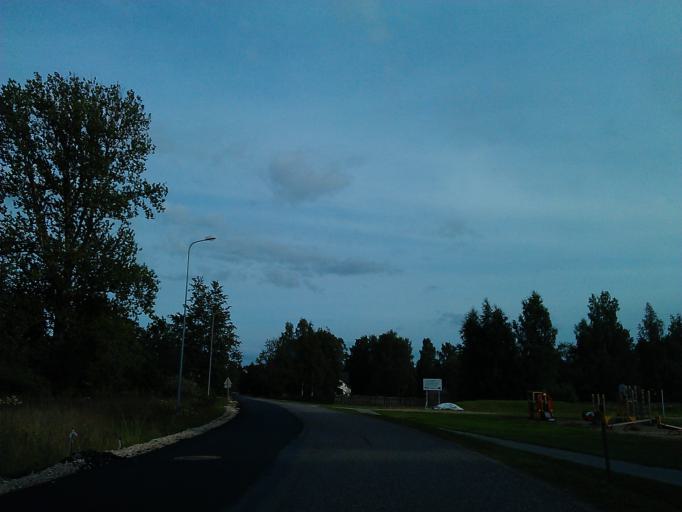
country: LV
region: Amatas Novads
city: Drabesi
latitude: 57.2050
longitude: 25.1658
